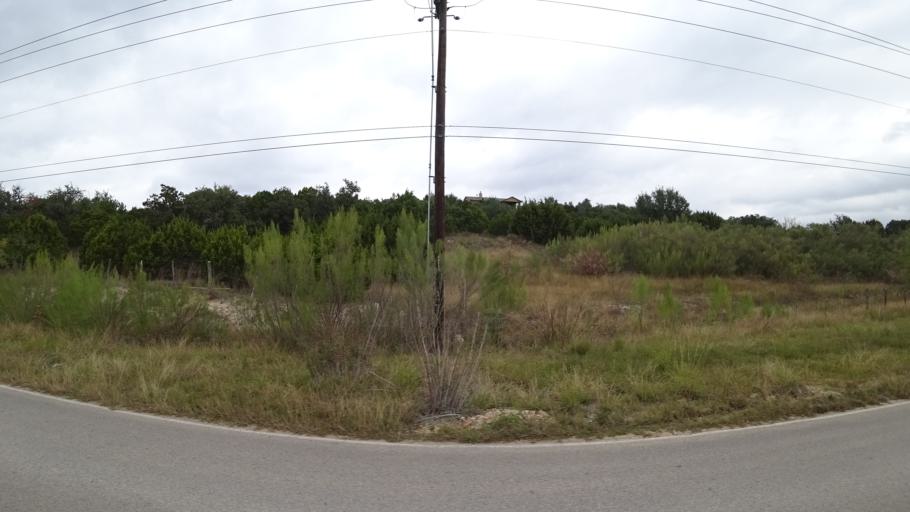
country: US
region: Texas
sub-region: Travis County
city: Bee Cave
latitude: 30.3380
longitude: -97.9180
